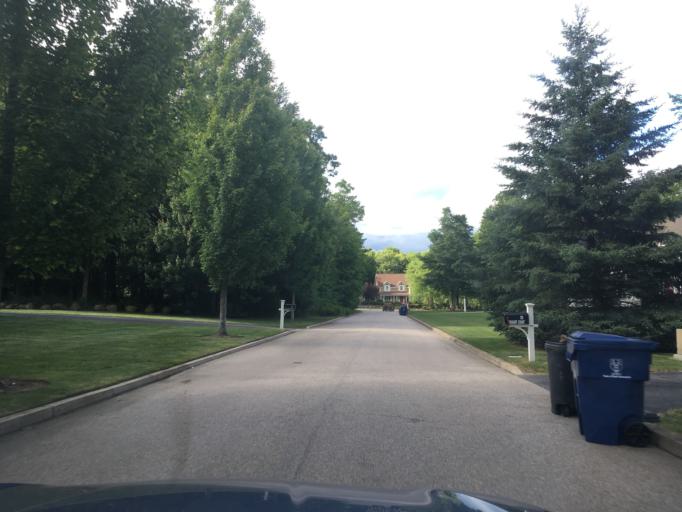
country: US
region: Rhode Island
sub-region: Washington County
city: Exeter
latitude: 41.6051
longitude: -71.5386
